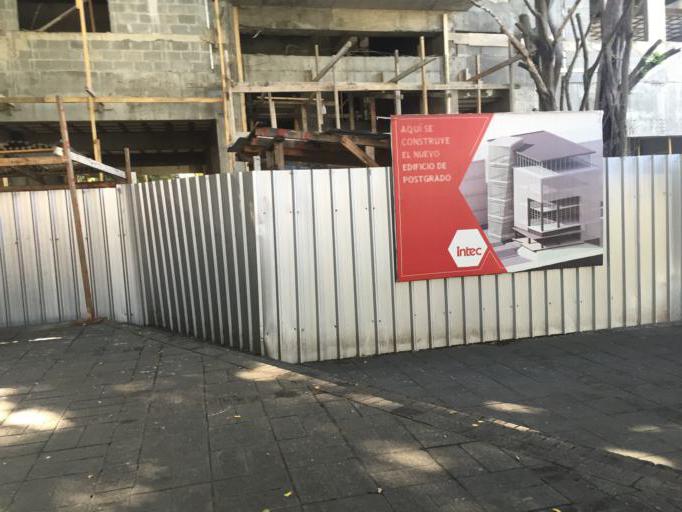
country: DO
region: Nacional
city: Santo Domingo
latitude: 18.4879
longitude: -69.9623
